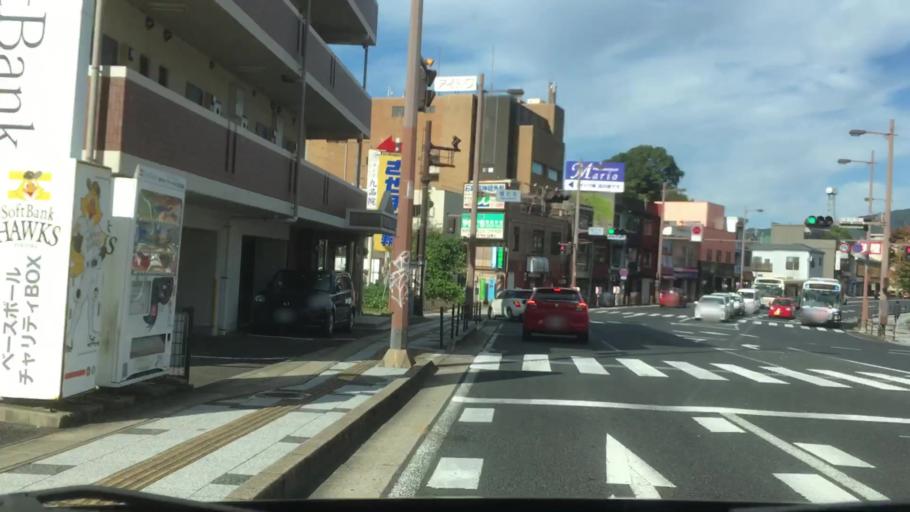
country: JP
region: Nagasaki
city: Sasebo
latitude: 33.1587
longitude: 129.7346
